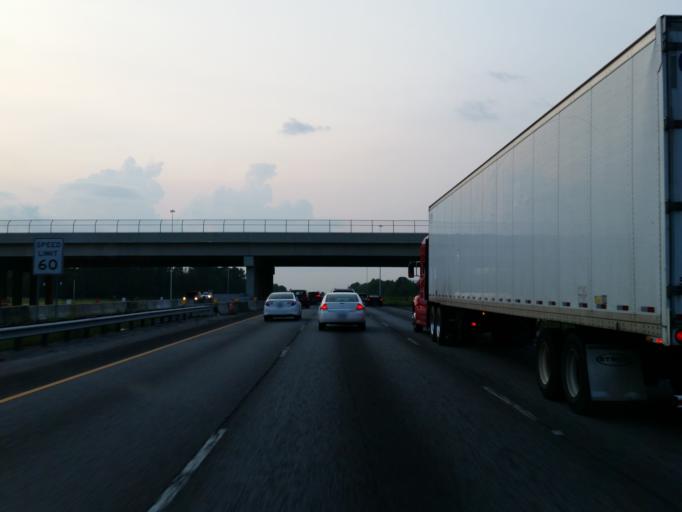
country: US
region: Georgia
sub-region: Henry County
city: Stockbridge
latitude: 33.4814
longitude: -84.2169
